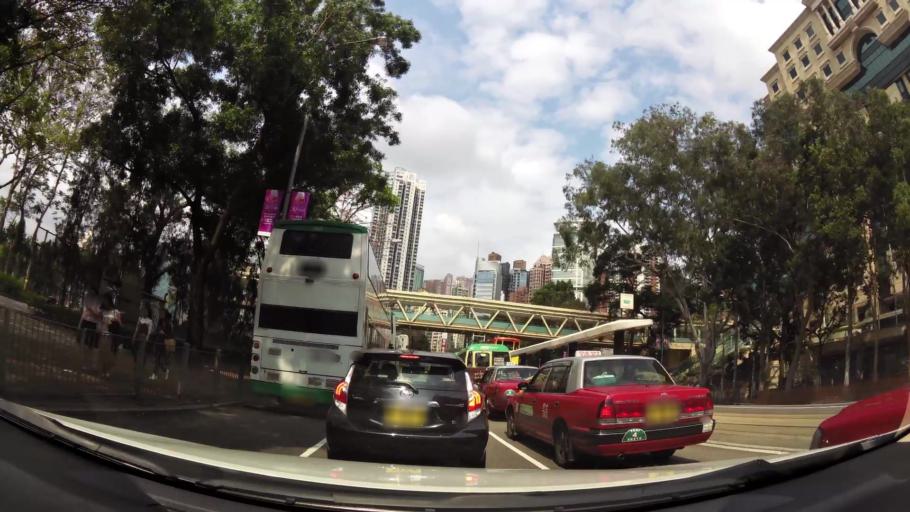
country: HK
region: Wanchai
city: Wan Chai
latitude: 22.2808
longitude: 114.1889
